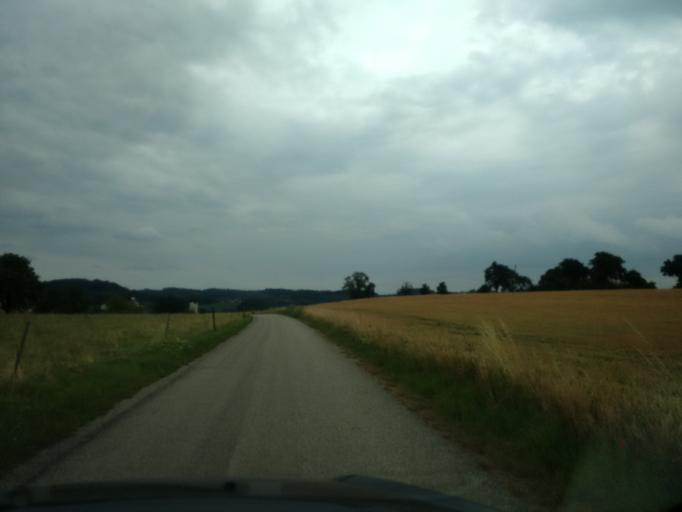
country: AT
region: Upper Austria
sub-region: Politischer Bezirk Grieskirchen
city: Bad Schallerbach
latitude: 48.2048
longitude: 13.9459
